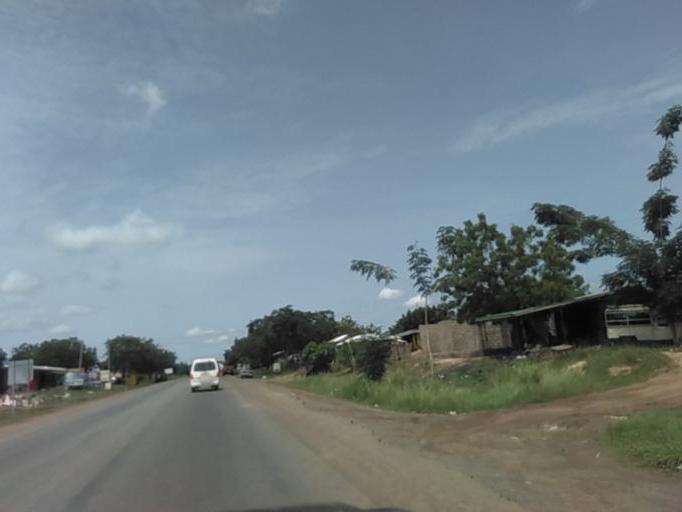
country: GH
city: Akropong
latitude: 6.1451
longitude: 0.0554
